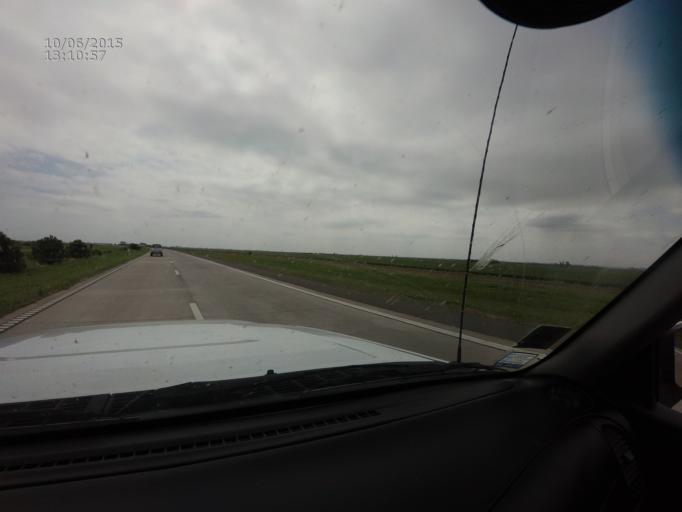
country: AR
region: Cordoba
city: General Roca
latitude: -32.7197
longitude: -61.8688
